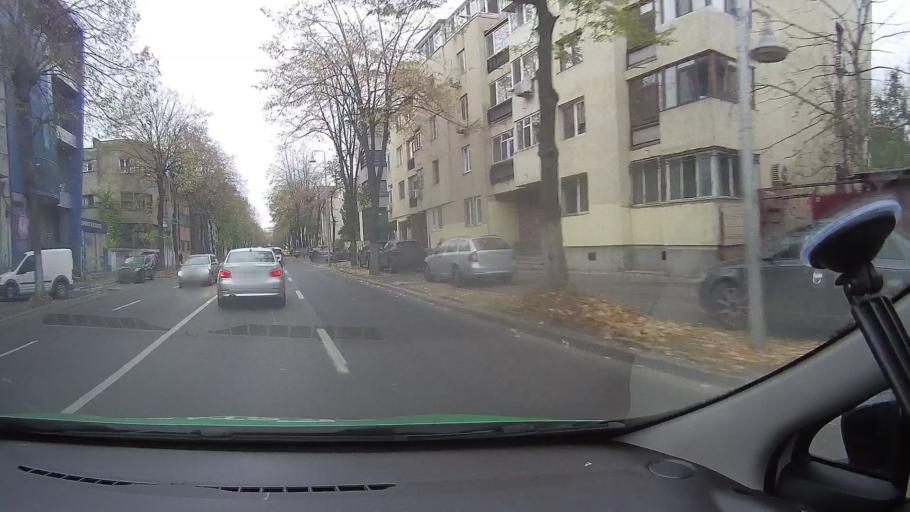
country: RO
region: Constanta
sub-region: Municipiul Constanta
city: Constanta
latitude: 44.1765
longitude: 28.6477
